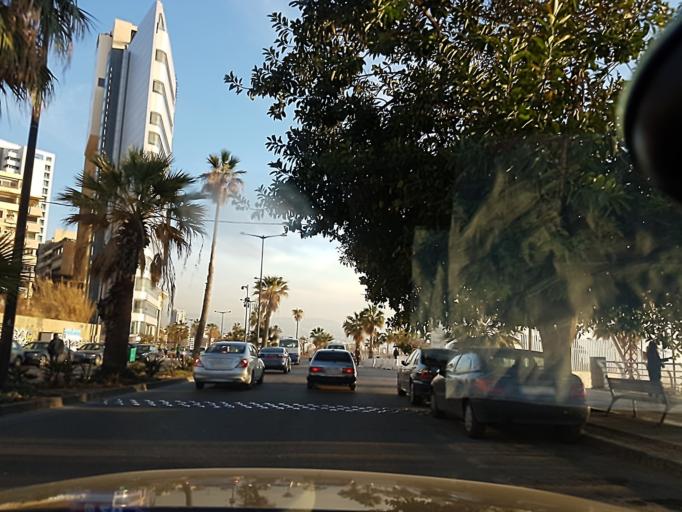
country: LB
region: Beyrouth
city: Ra's Bayrut
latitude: 33.8872
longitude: 35.4736
